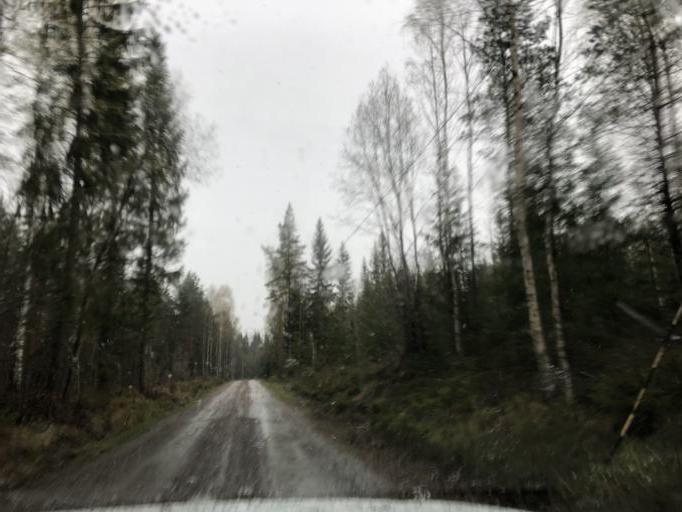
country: SE
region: Uppsala
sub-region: Heby Kommun
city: Tarnsjo
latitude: 60.2059
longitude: 16.8913
